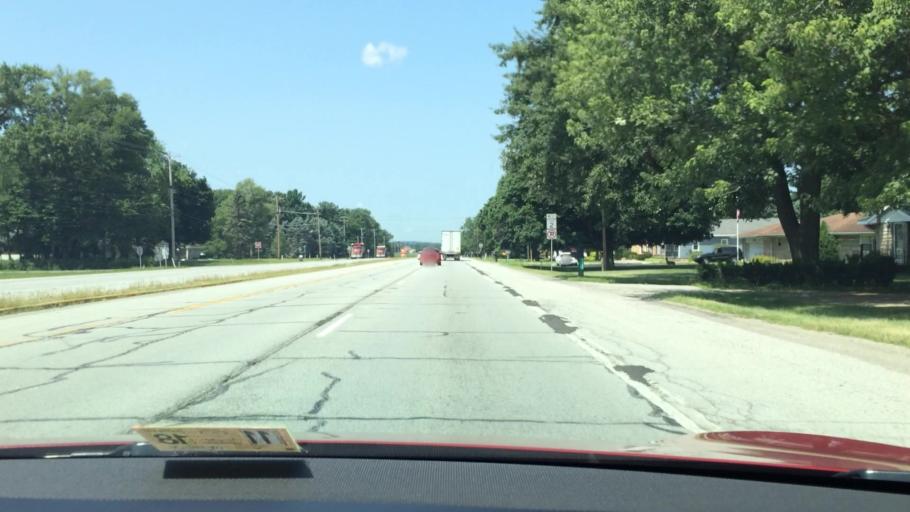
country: US
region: Indiana
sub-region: Saint Joseph County
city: South Bend
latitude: 41.6720
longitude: -86.3808
